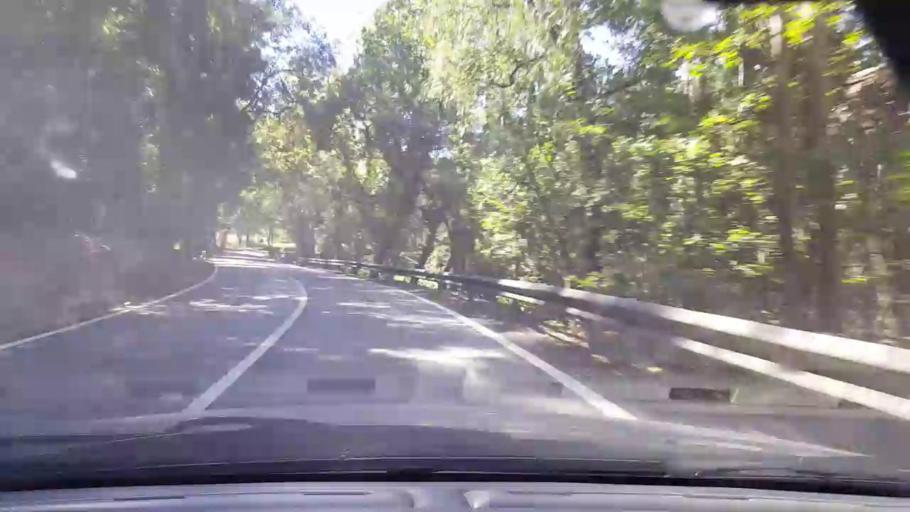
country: PT
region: Braga
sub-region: Vila Nova de Famalicao
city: Ribeirao
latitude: 41.3393
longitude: -8.6271
